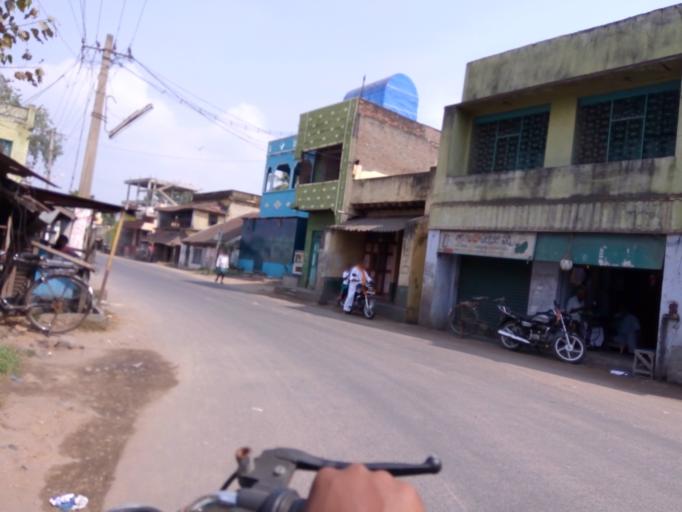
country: IN
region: Andhra Pradesh
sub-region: Prakasam
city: Chirala
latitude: 15.8501
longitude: 80.3891
